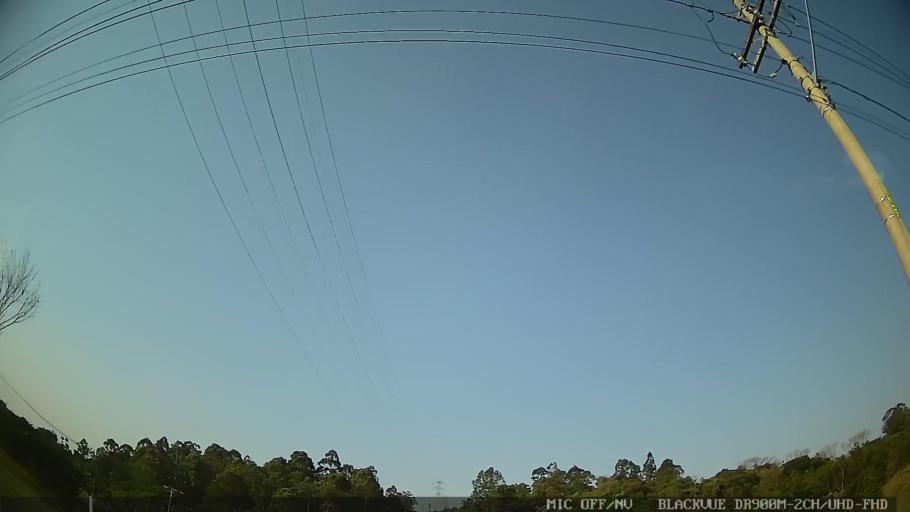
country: BR
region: Sao Paulo
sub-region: Itatiba
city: Itatiba
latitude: -23.0288
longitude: -46.8352
